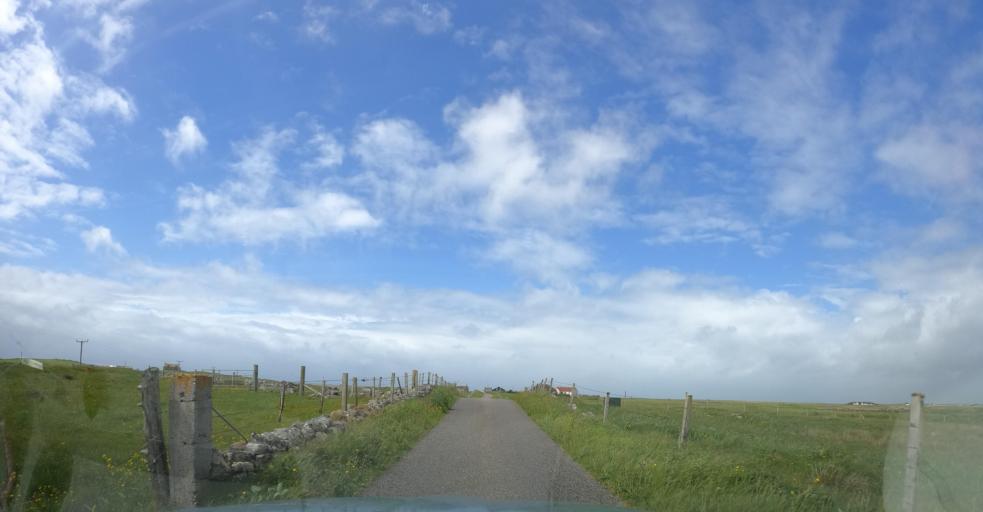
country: GB
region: Scotland
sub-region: Eilean Siar
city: Isle of South Uist
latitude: 57.2767
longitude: -7.4111
